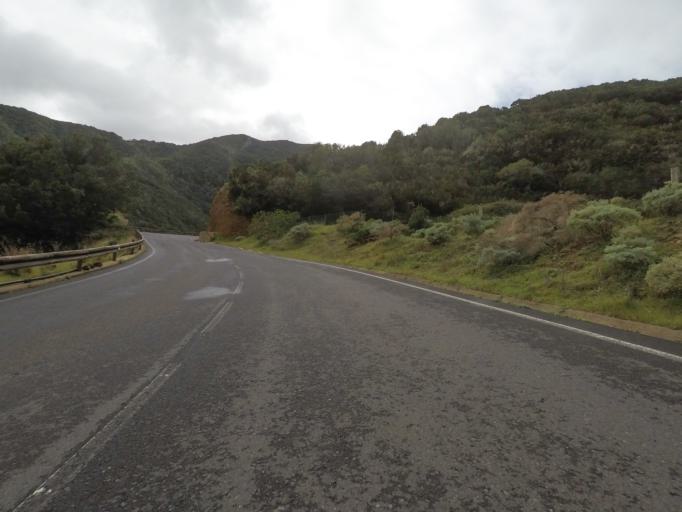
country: ES
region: Canary Islands
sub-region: Provincia de Santa Cruz de Tenerife
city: Vallehermosa
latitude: 28.1594
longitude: -17.2863
